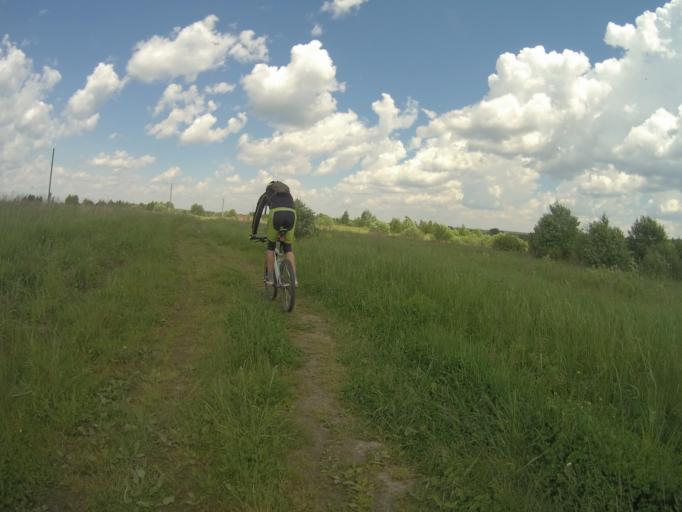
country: RU
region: Vladimir
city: Raduzhnyy
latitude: 56.0022
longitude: 40.2176
